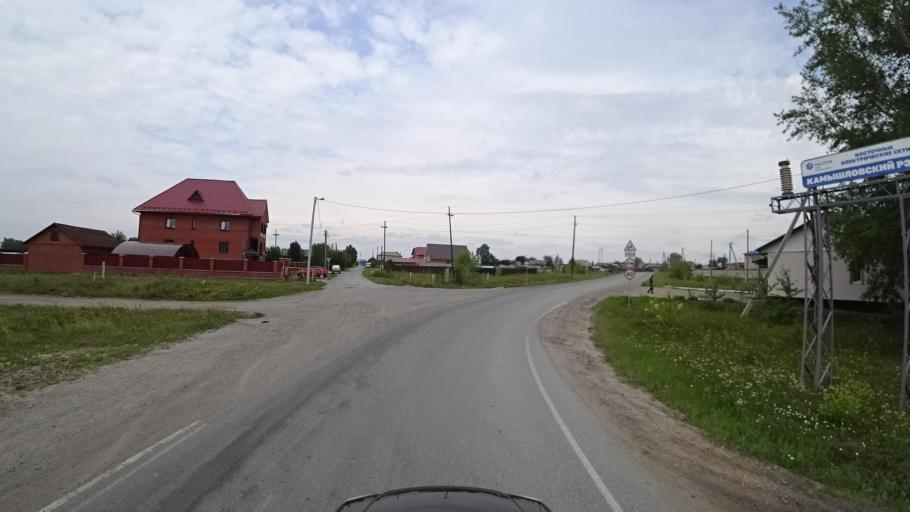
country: RU
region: Sverdlovsk
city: Kamyshlov
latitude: 56.8479
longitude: 62.7438
